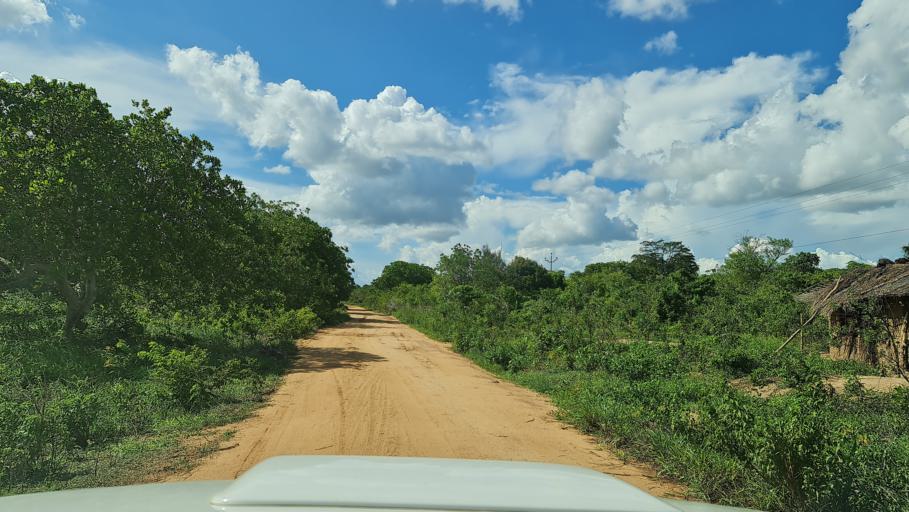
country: MZ
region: Nampula
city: Ilha de Mocambique
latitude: -15.4293
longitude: 40.2729
